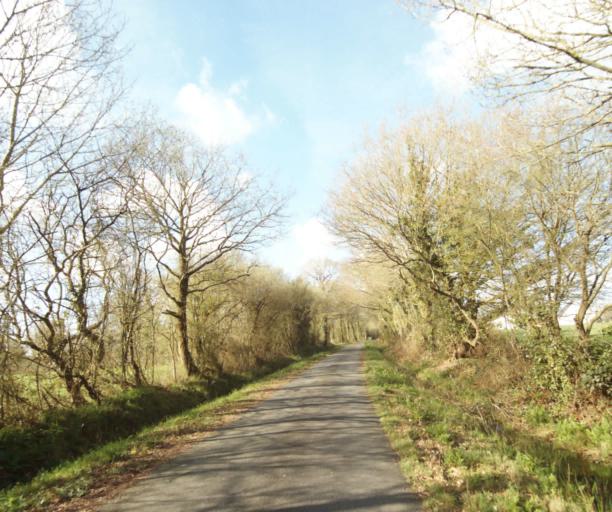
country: FR
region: Pays de la Loire
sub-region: Departement de la Loire-Atlantique
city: Bouvron
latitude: 47.4041
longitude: -1.8362
